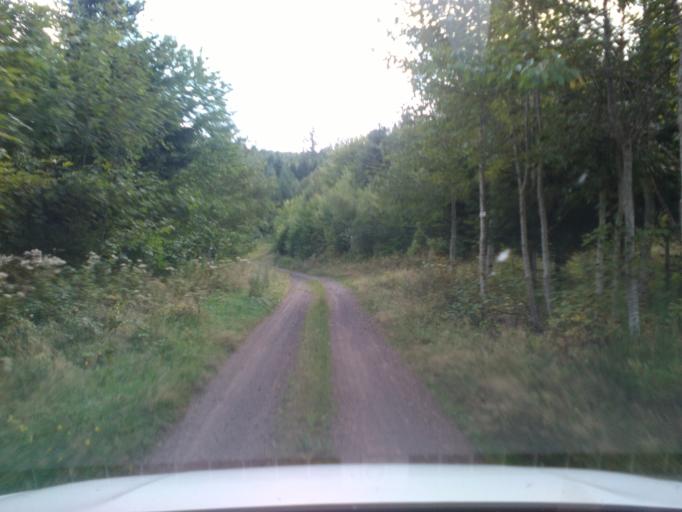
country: FR
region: Lorraine
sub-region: Departement des Vosges
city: Senones
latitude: 48.3509
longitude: 7.0369
